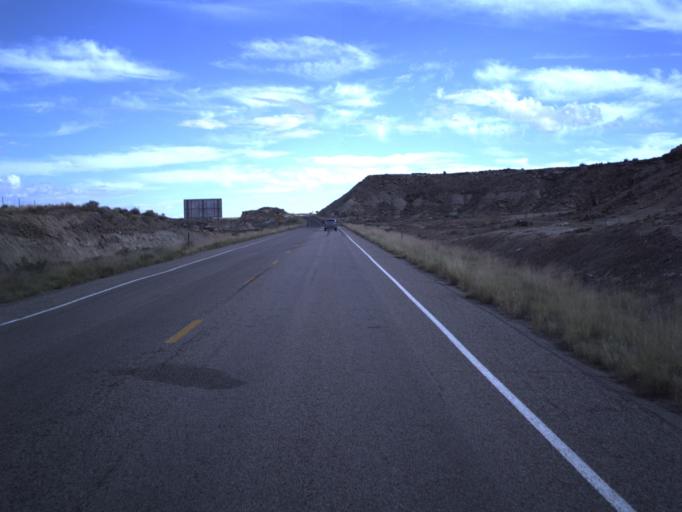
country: US
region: Colorado
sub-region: Montezuma County
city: Towaoc
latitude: 37.1518
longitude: -109.0476
